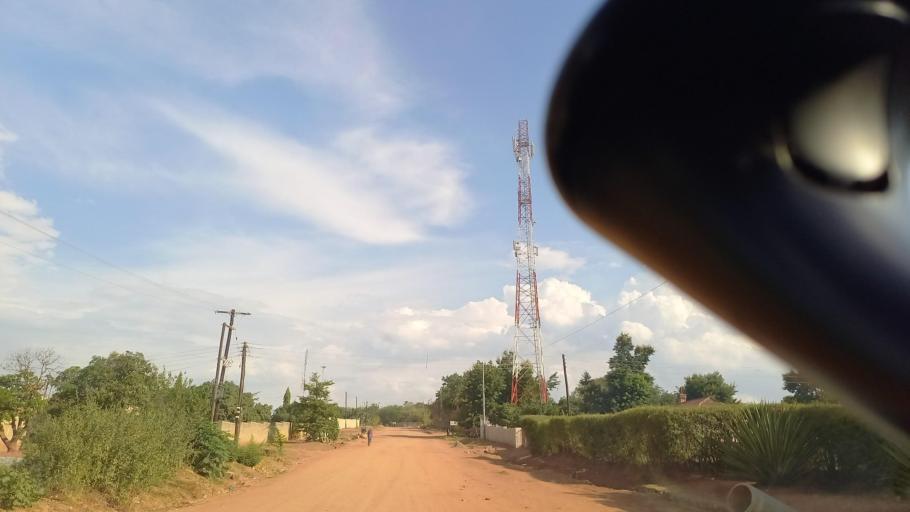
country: ZM
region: Southern
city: Mazabuka
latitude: -15.8616
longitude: 27.7608
